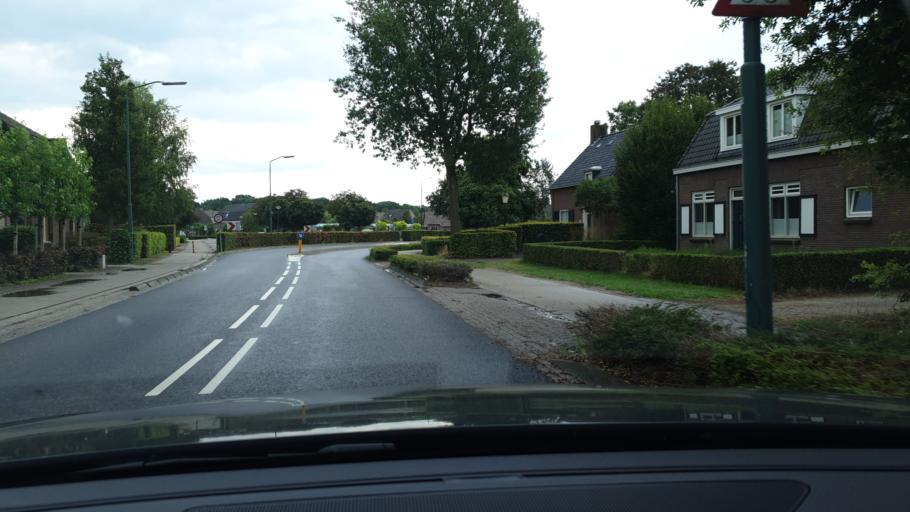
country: NL
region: North Brabant
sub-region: Gemeente Sint-Oedenrode
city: Sint-Oedenrode
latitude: 51.5587
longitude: 5.4464
